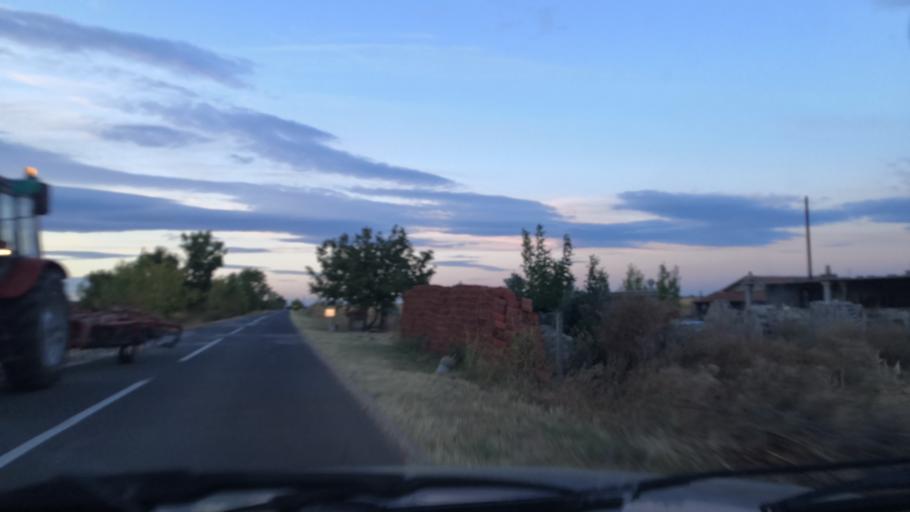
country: RS
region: Central Serbia
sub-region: Borski Okrug
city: Negotin
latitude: 44.2797
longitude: 22.5564
